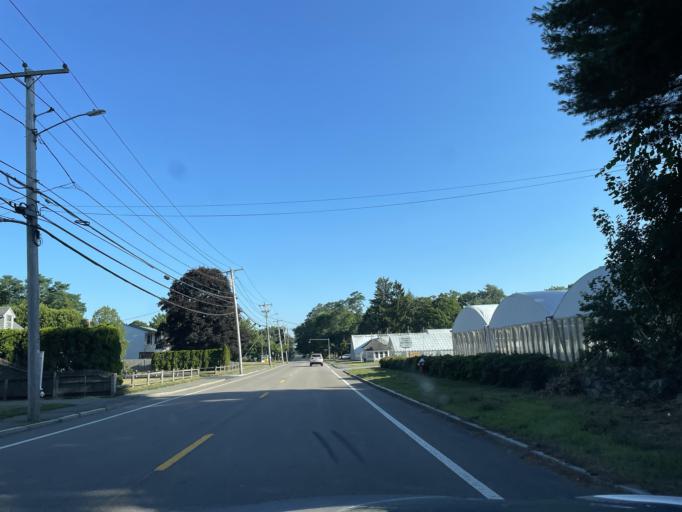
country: US
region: Massachusetts
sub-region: Bristol County
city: Mansfield
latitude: 42.0458
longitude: -71.2350
